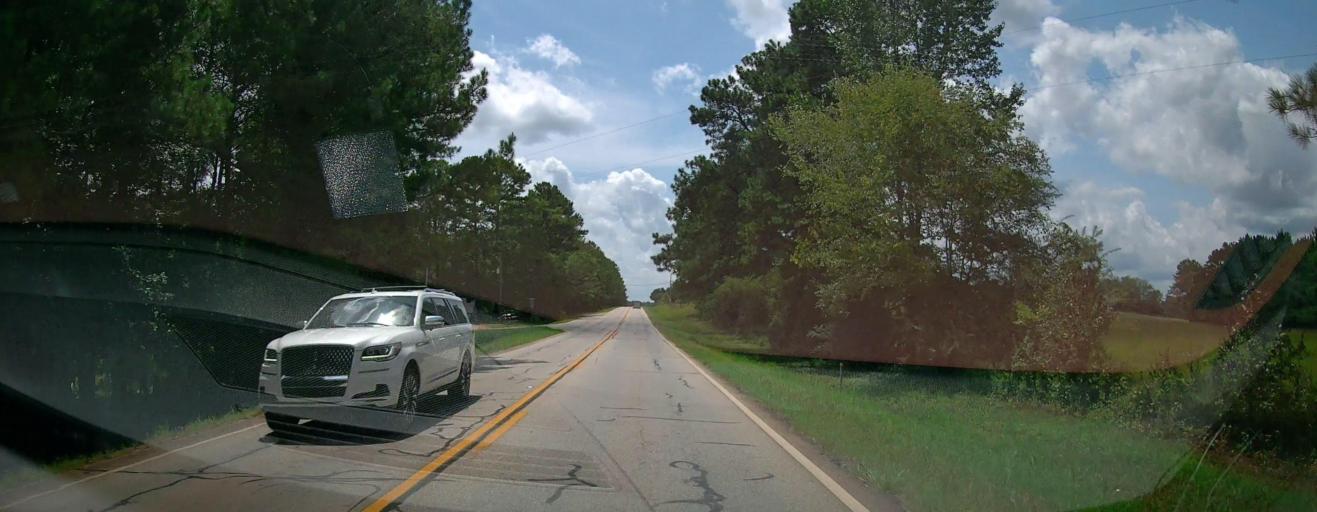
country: US
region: Georgia
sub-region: Troup County
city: Hogansville
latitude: 33.2327
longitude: -84.9573
